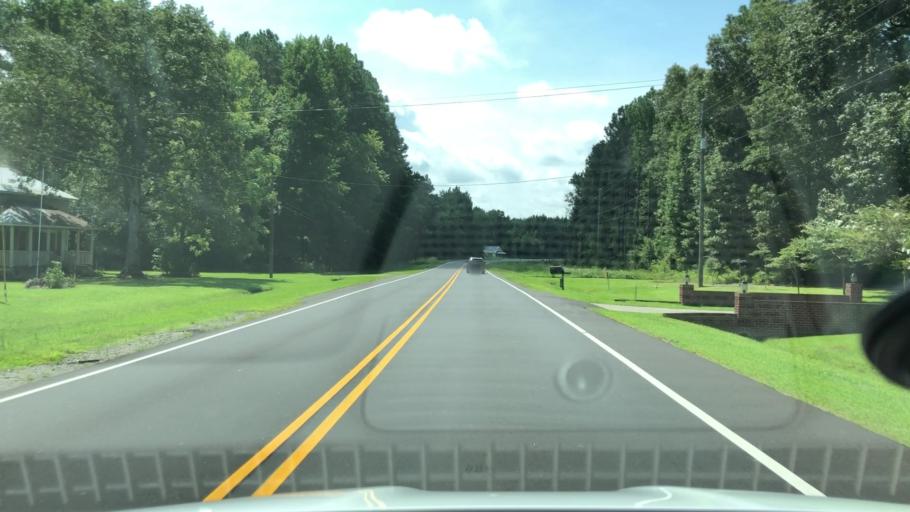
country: US
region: North Carolina
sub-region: Martin County
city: Williamston
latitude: 35.7368
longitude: -77.0756
